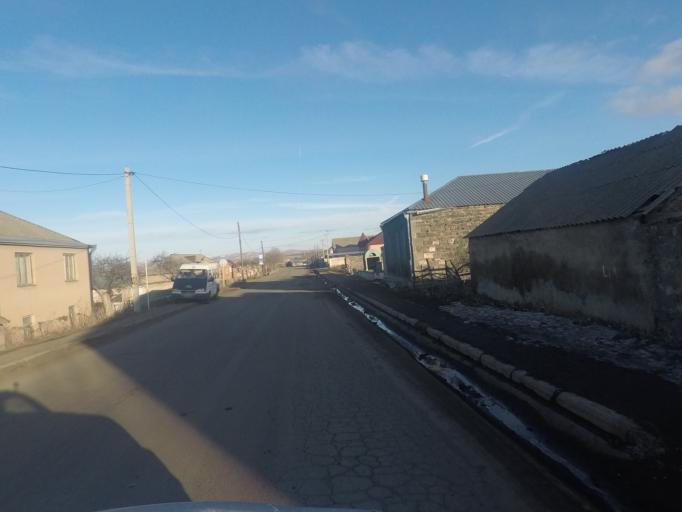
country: GE
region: Kvemo Kartli
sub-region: Tsalka
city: Tsalka
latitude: 41.5996
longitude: 44.0072
